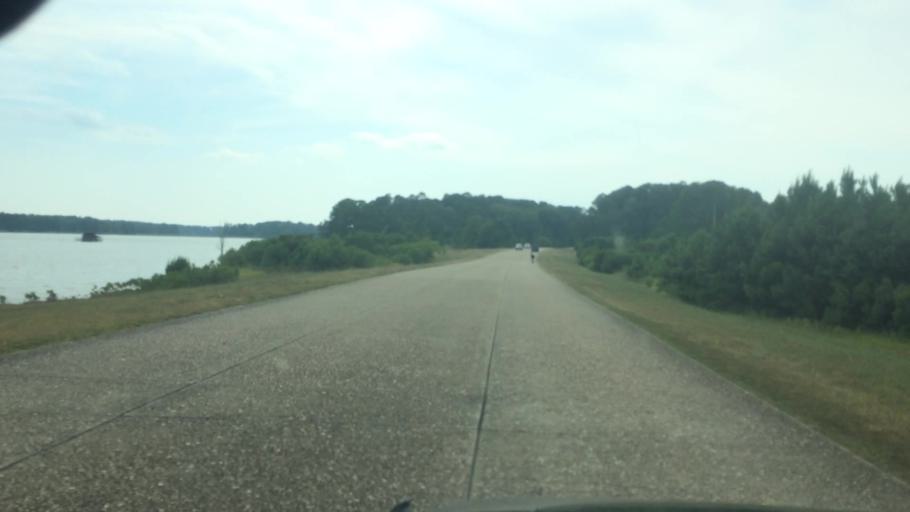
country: US
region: Virginia
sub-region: James City County
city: Williamsburg
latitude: 37.2135
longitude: -76.7340
